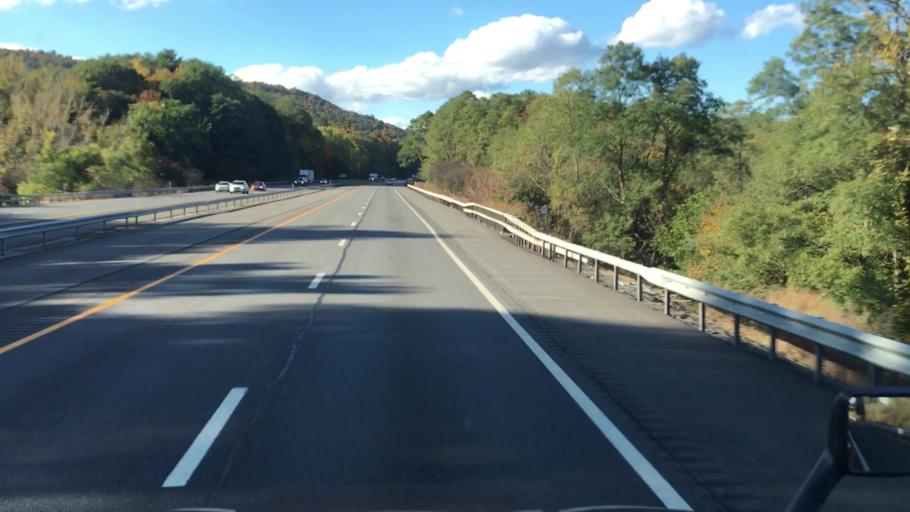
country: US
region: New York
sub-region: Schenectady County
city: Scotia
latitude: 42.8499
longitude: -74.0261
